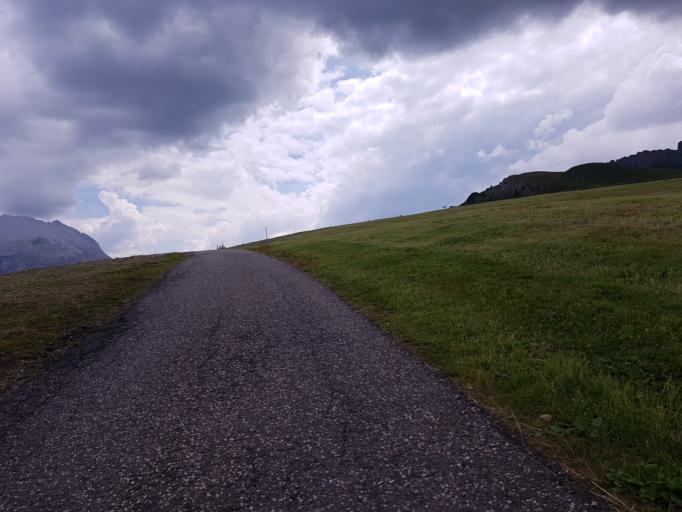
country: IT
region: Trentino-Alto Adige
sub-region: Bolzano
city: Ortisei
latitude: 46.5267
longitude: 11.6304
